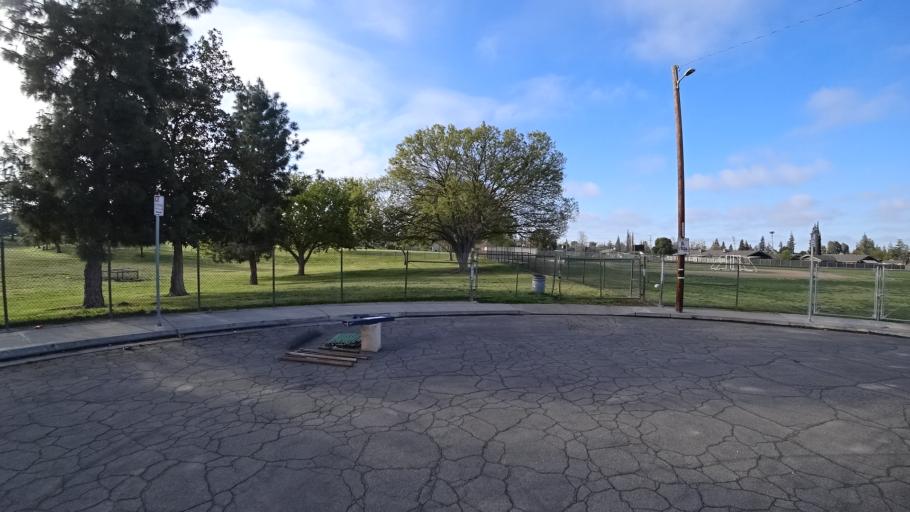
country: US
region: California
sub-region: Fresno County
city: Fresno
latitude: 36.8173
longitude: -119.7971
